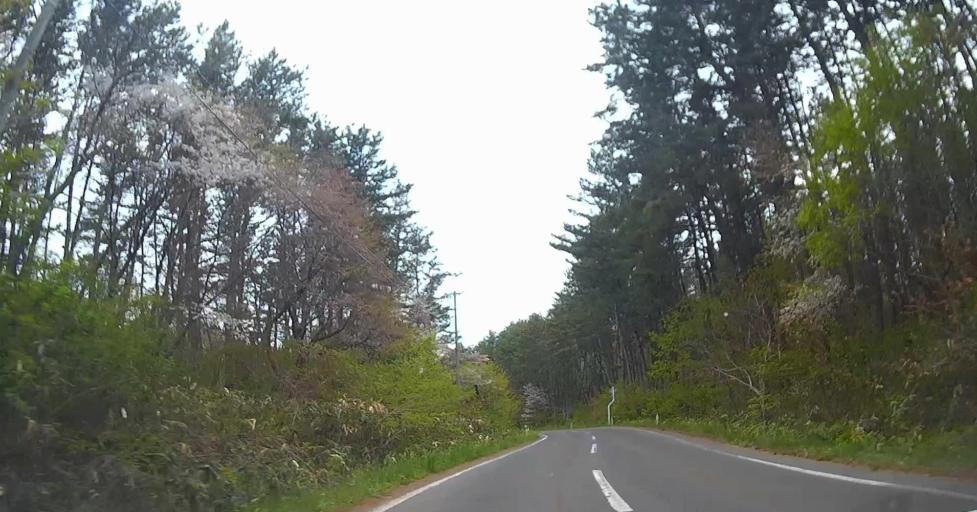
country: JP
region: Aomori
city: Shimokizukuri
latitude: 40.9373
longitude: 140.3322
